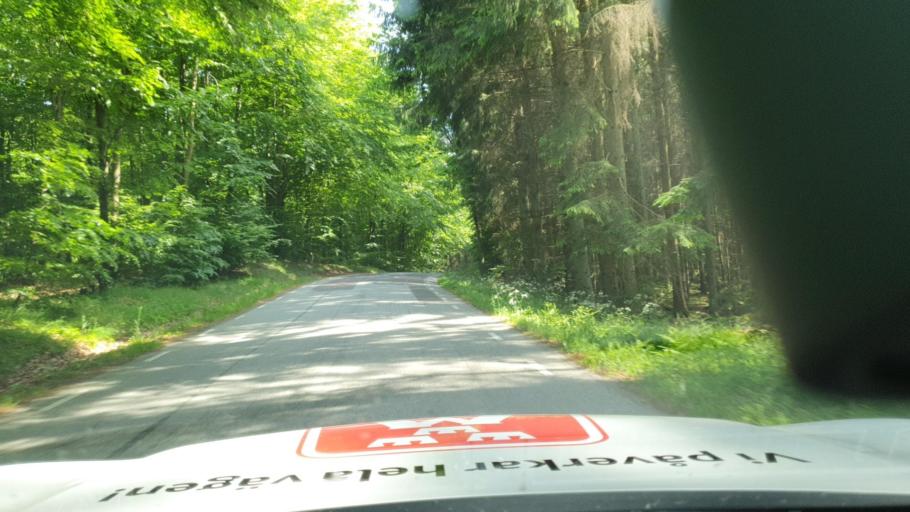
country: SE
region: Skane
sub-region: Svedala Kommun
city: Svedala
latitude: 55.5288
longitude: 13.2844
